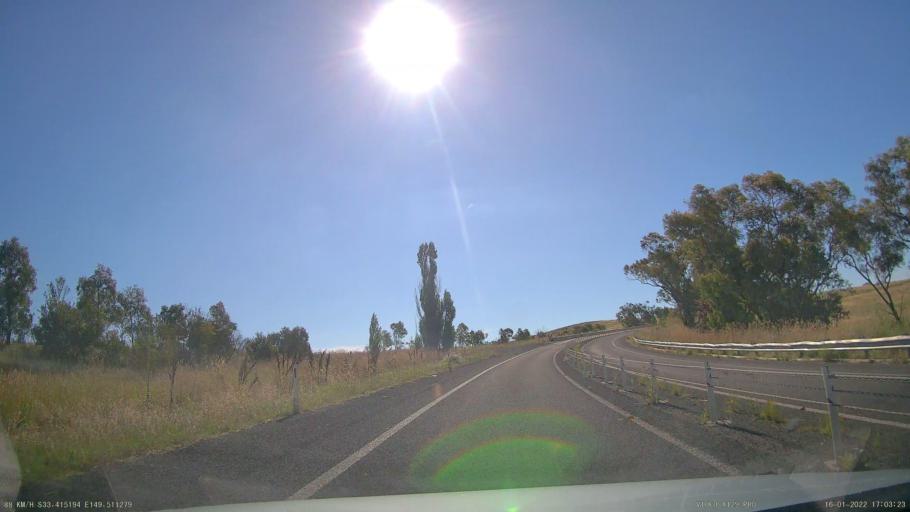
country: AU
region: New South Wales
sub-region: Bathurst Regional
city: Eglinton
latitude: -33.4152
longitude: 149.5113
